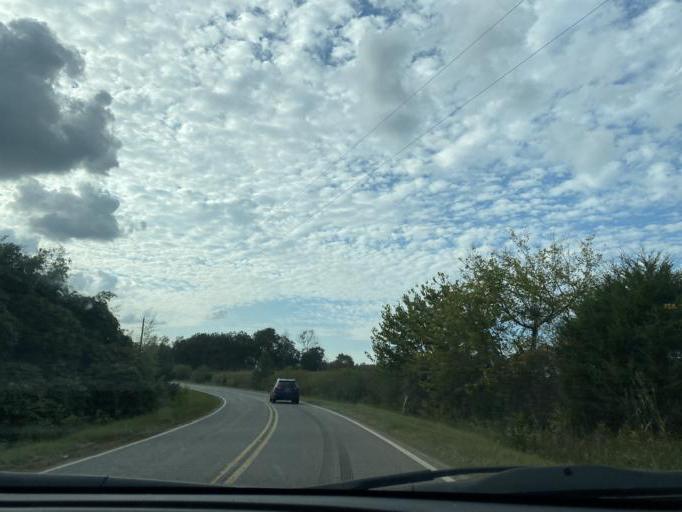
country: US
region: South Carolina
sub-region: Cherokee County
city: Gaffney
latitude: 35.0724
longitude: -81.7128
